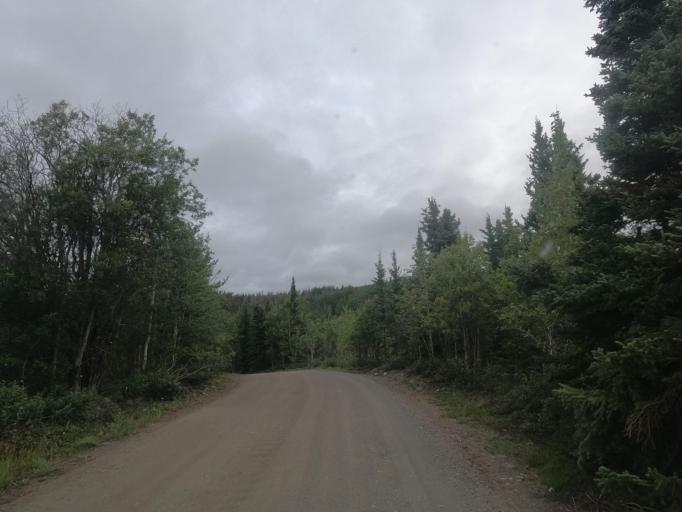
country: CA
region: Yukon
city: Haines Junction
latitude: 60.1096
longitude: -136.9394
